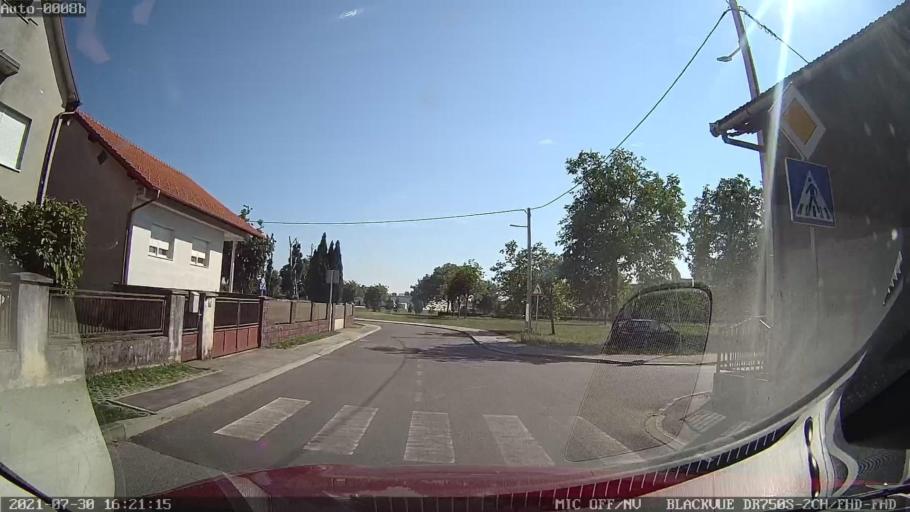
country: HR
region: Medimurska
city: Kursanec
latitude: 46.2949
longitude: 16.4061
